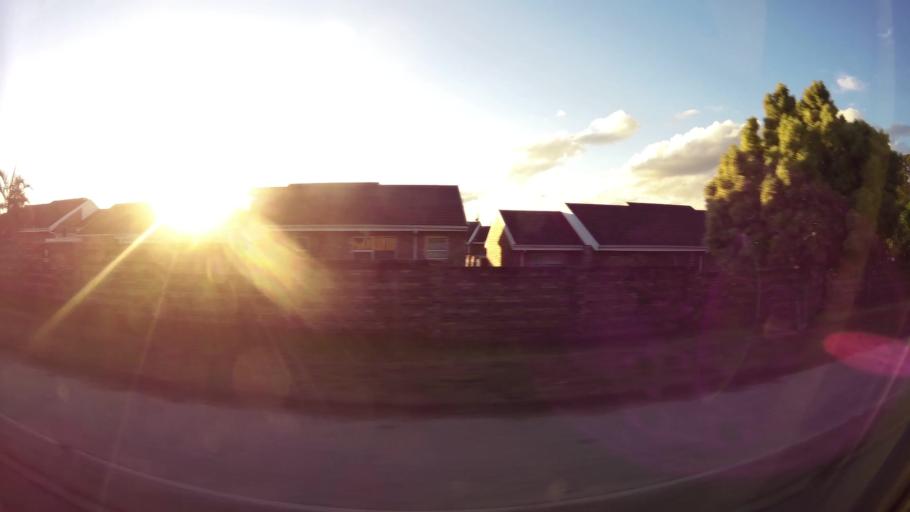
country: ZA
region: Eastern Cape
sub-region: Nelson Mandela Bay Metropolitan Municipality
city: Port Elizabeth
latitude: -33.9644
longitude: 25.5028
